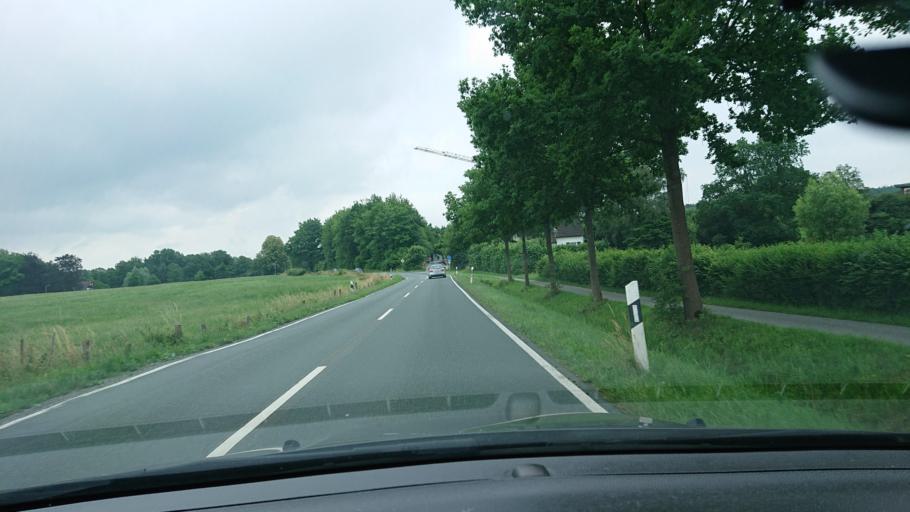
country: DE
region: North Rhine-Westphalia
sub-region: Regierungsbezirk Arnsberg
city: Mohnesee
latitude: 51.4731
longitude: 8.2290
